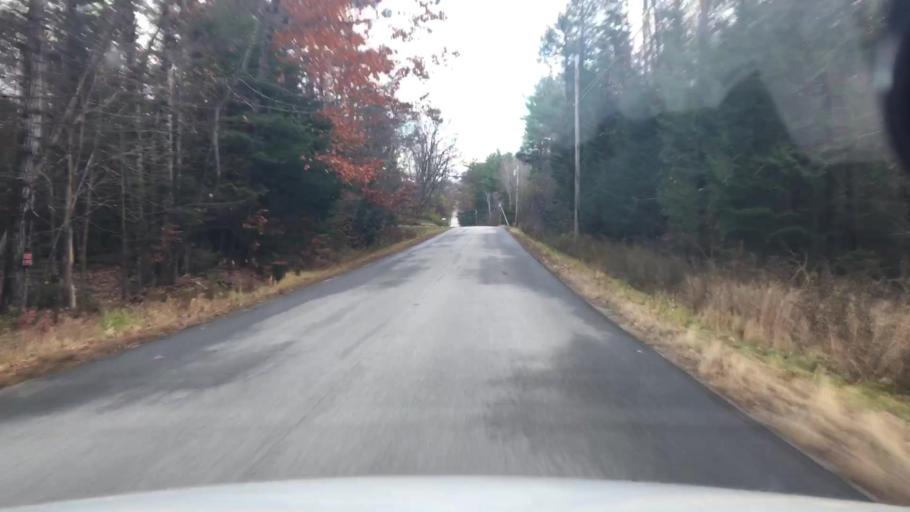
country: US
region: Maine
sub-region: Somerset County
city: Saint Albans
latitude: 44.9090
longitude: -69.4445
